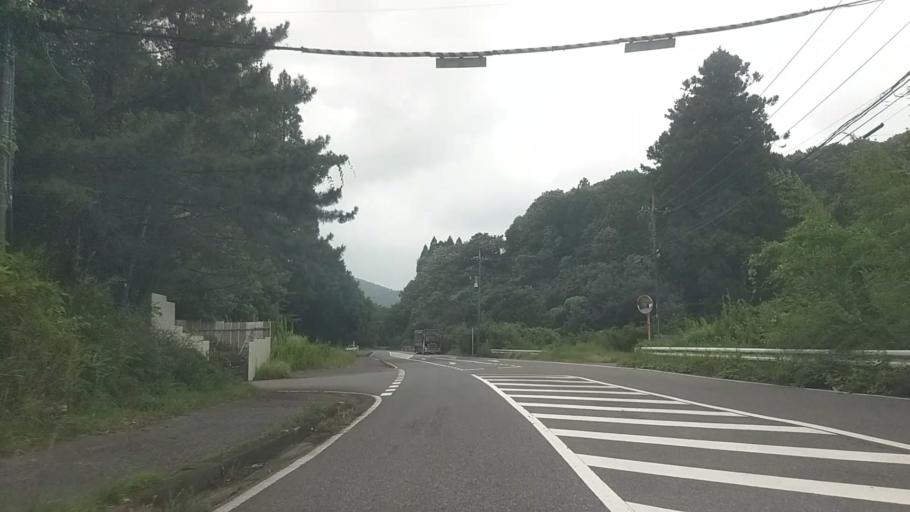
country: JP
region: Chiba
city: Kawaguchi
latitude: 35.2404
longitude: 140.0352
